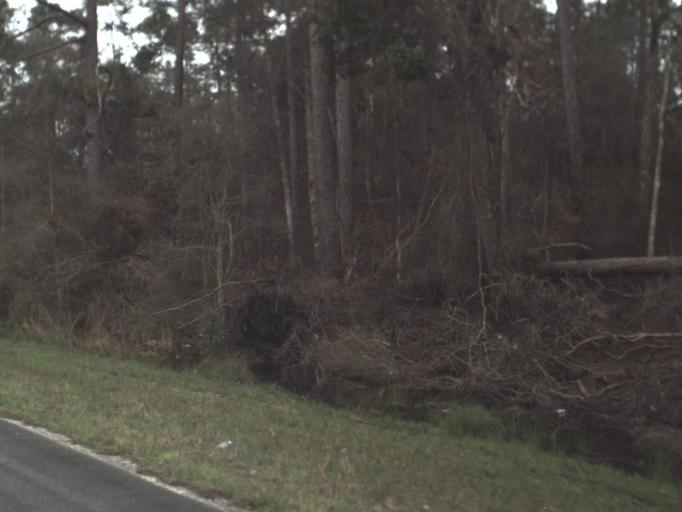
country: US
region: Florida
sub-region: Gadsden County
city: Midway
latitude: 30.3563
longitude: -84.5256
